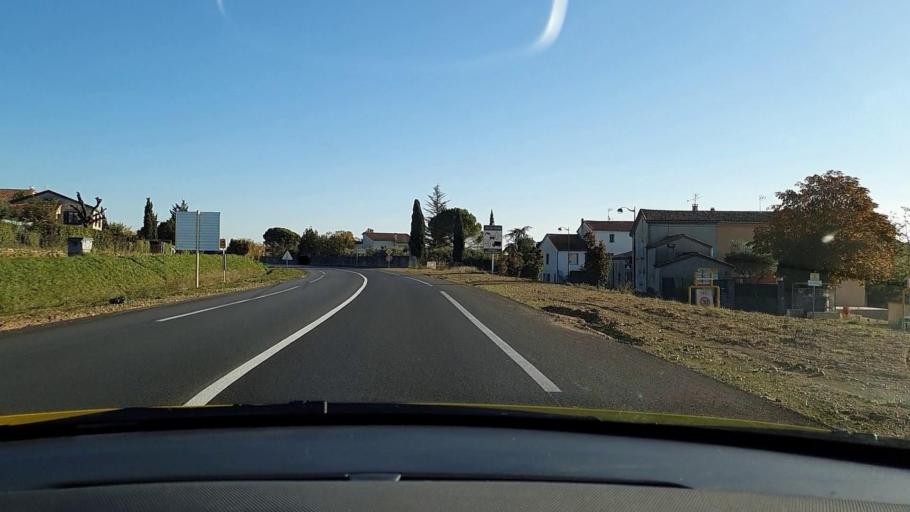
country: FR
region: Languedoc-Roussillon
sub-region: Departement du Gard
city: Saint-Julien-les-Rosiers
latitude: 44.1582
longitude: 4.1147
